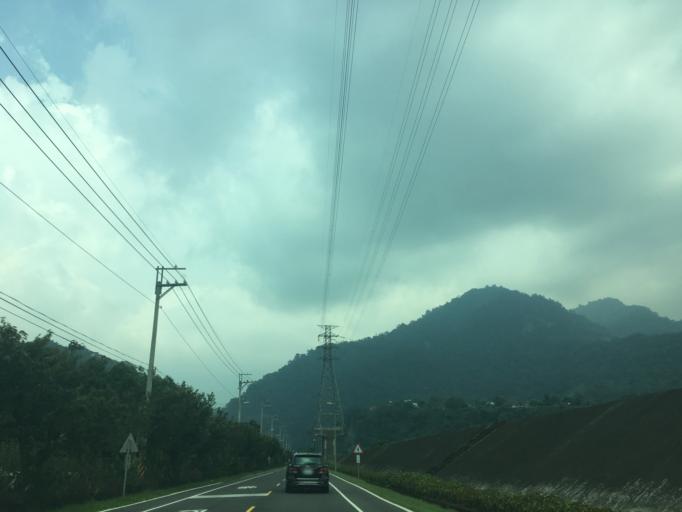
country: TW
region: Taiwan
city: Fengyuan
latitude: 24.2944
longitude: 120.9010
